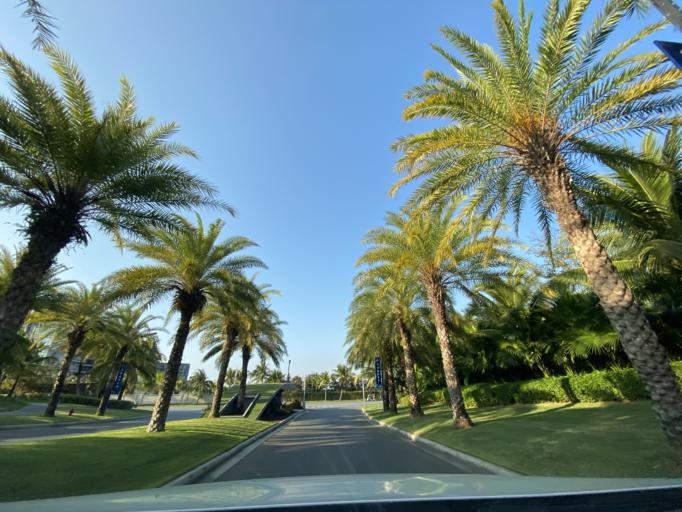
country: CN
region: Hainan
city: Xincun
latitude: 18.4213
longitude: 109.9482
